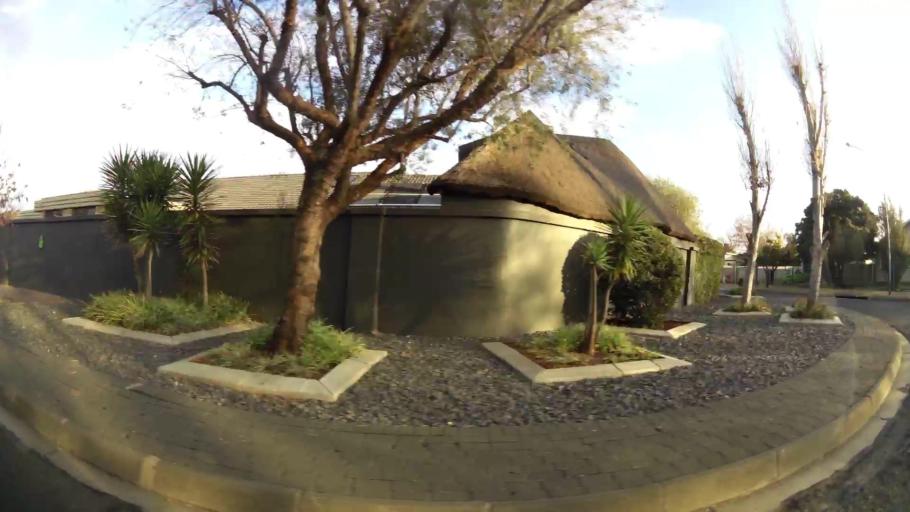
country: ZA
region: Orange Free State
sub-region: Mangaung Metropolitan Municipality
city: Bloemfontein
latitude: -29.1430
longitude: 26.1870
